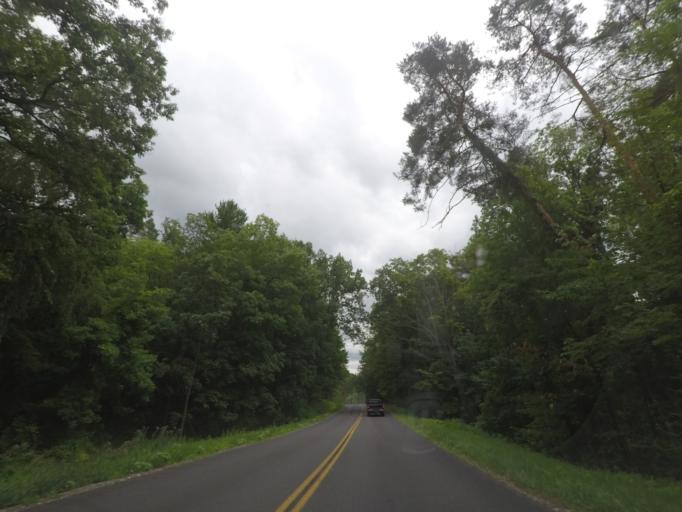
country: US
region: New York
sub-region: Rensselaer County
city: Poestenkill
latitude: 42.8299
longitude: -73.5211
